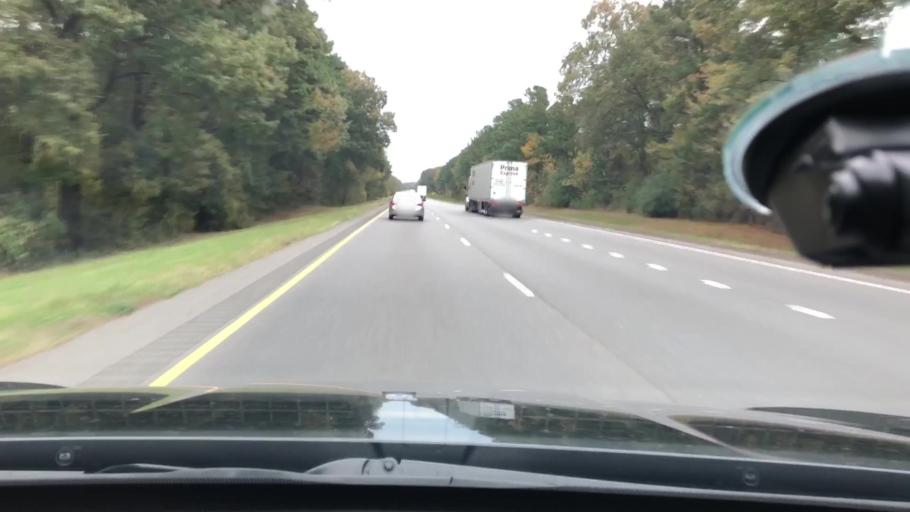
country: US
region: Arkansas
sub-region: Hempstead County
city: Hope
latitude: 33.6519
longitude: -93.6664
